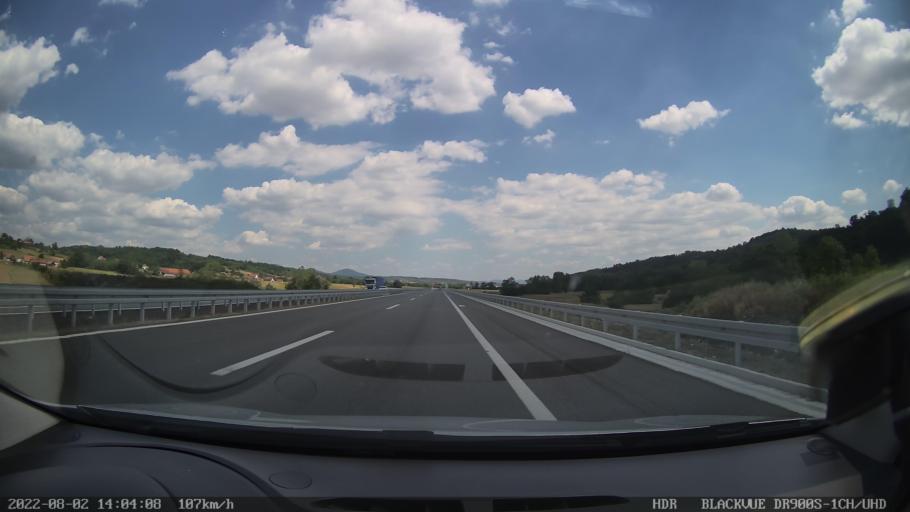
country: RS
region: Central Serbia
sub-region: Moravicki Okrug
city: Cacak
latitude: 43.9238
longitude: 20.3649
